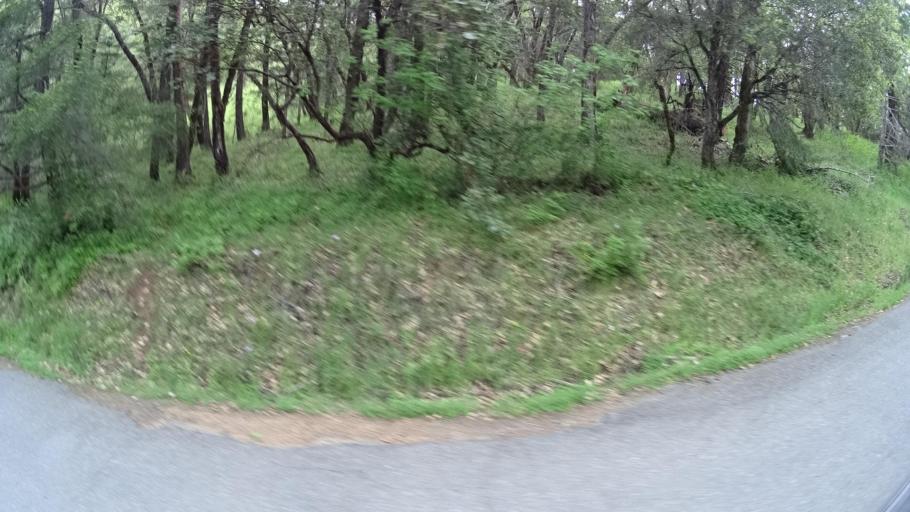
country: US
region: California
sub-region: Humboldt County
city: Redway
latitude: 40.1841
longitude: -123.5797
